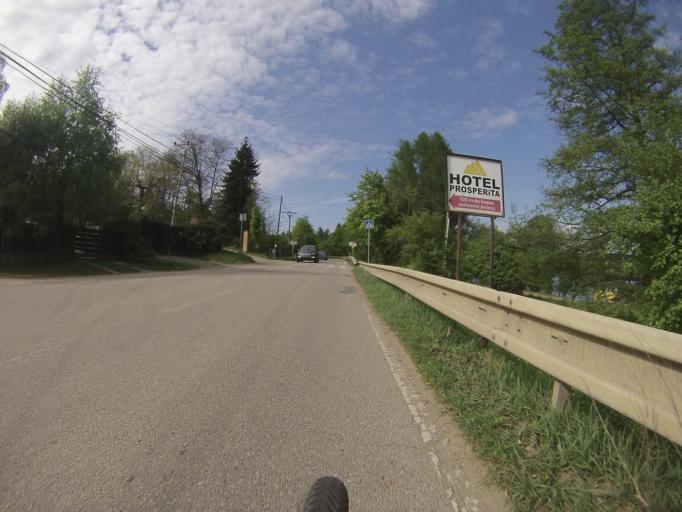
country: CZ
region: South Moravian
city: Kurim
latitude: 49.2375
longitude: 16.5048
